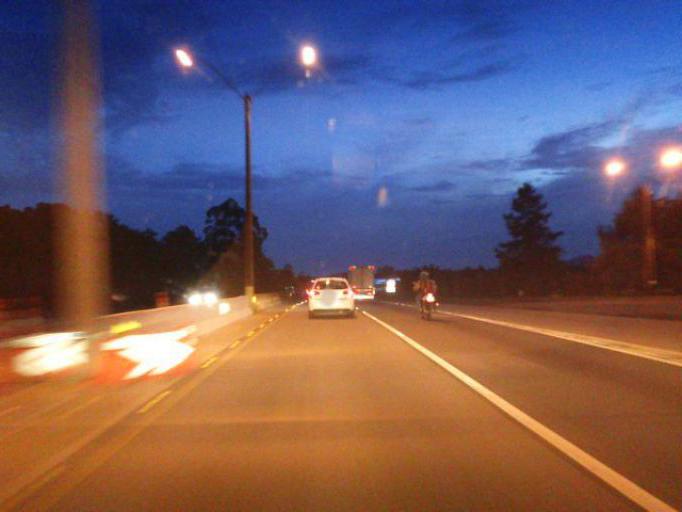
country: BR
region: Santa Catarina
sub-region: Barra Velha
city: Barra Velha
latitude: -26.6107
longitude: -48.7221
